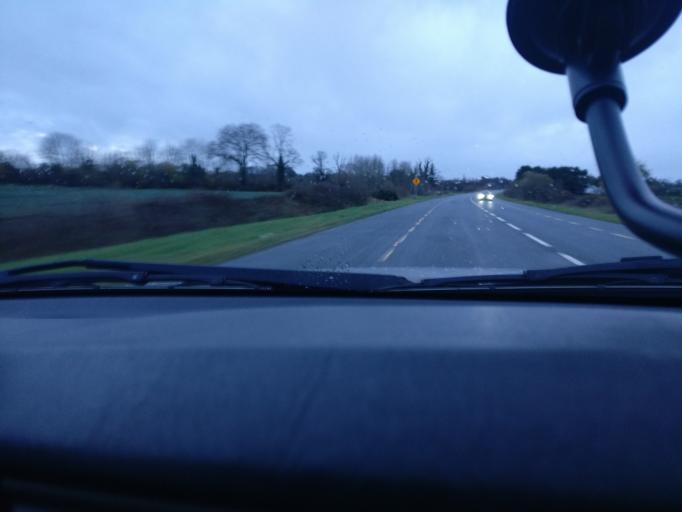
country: IE
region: Connaught
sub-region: County Galway
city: Ballinasloe
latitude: 53.2929
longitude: -8.3310
